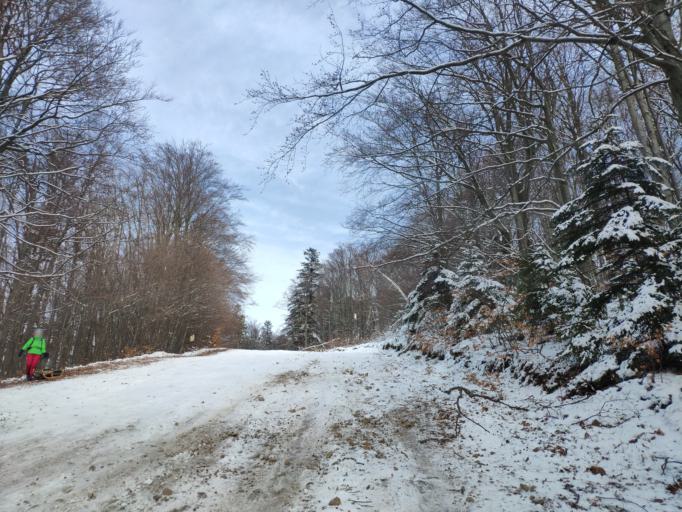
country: SK
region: Kosicky
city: Gelnica
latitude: 48.7647
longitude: 20.9925
